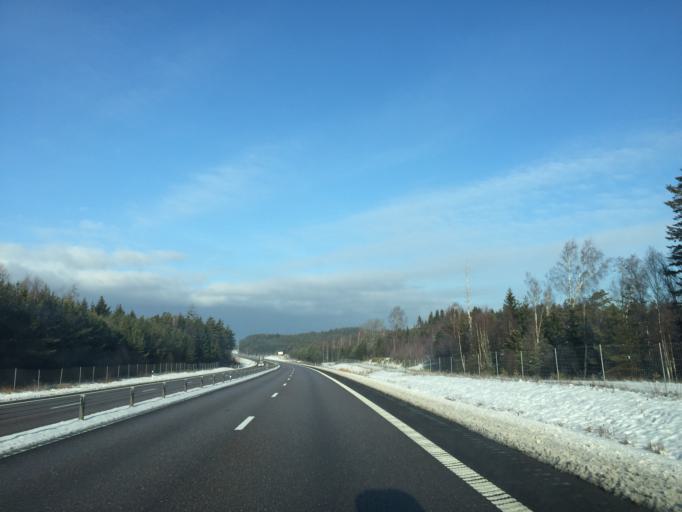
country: SE
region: Vaestra Goetaland
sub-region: Tanums Kommun
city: Tanumshede
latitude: 58.7450
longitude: 11.2984
